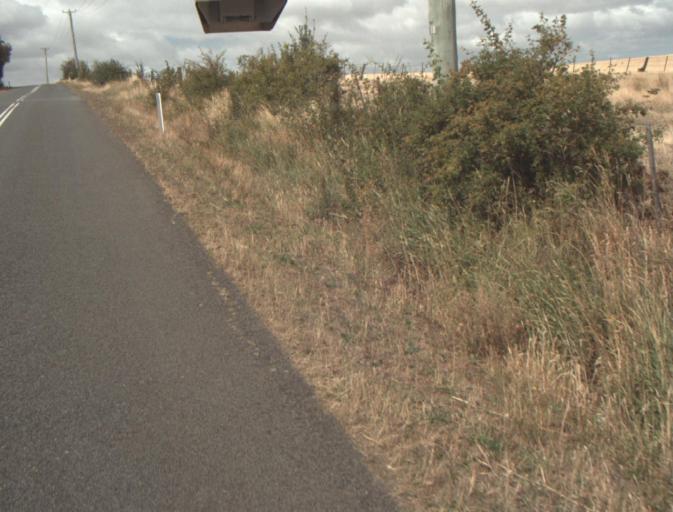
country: AU
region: Tasmania
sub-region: Northern Midlands
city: Evandale
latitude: -41.5104
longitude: 147.2882
